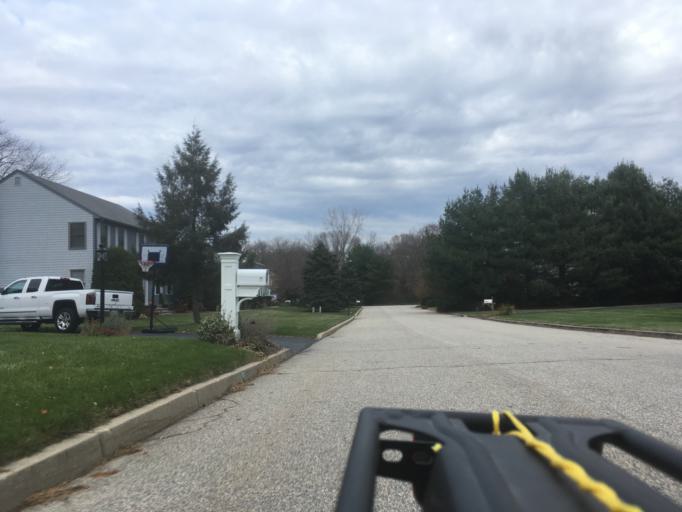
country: US
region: Rhode Island
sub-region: Kent County
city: East Greenwich
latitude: 41.6515
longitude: -71.4657
